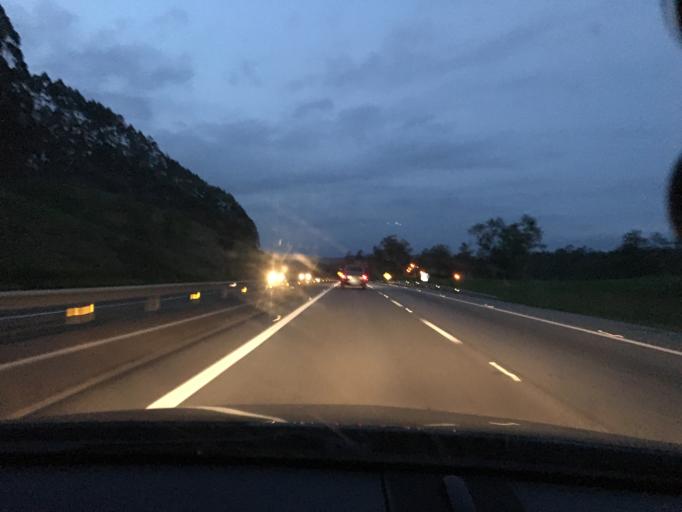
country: BR
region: Sao Paulo
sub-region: Santa Isabel
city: Santa Isabel
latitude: -23.3574
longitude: -46.1259
